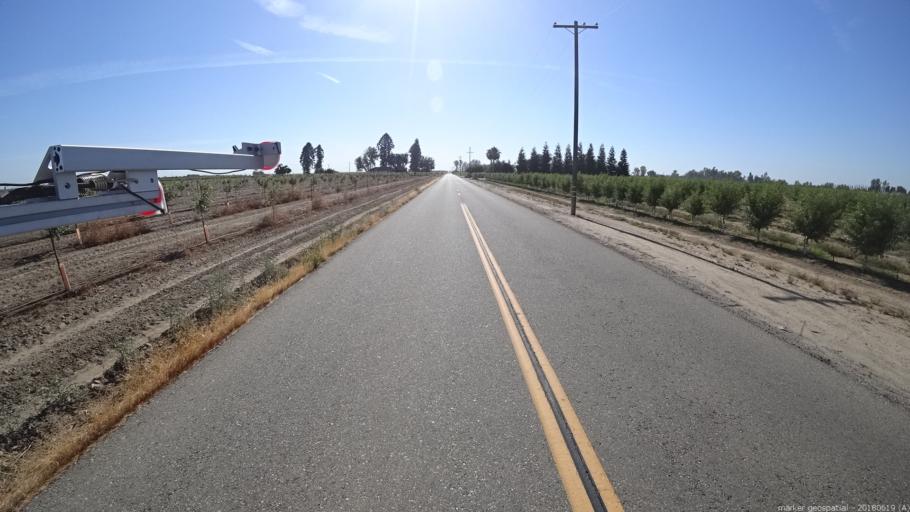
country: US
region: California
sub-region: Fresno County
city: Biola
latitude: 36.8296
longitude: -120.0643
